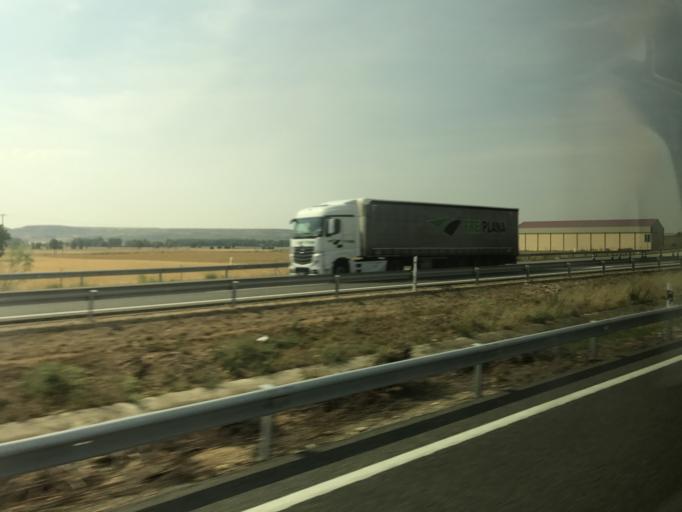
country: ES
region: Castille and Leon
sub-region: Provincia de Burgos
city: Villazopeque
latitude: 42.2052
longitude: -4.0160
